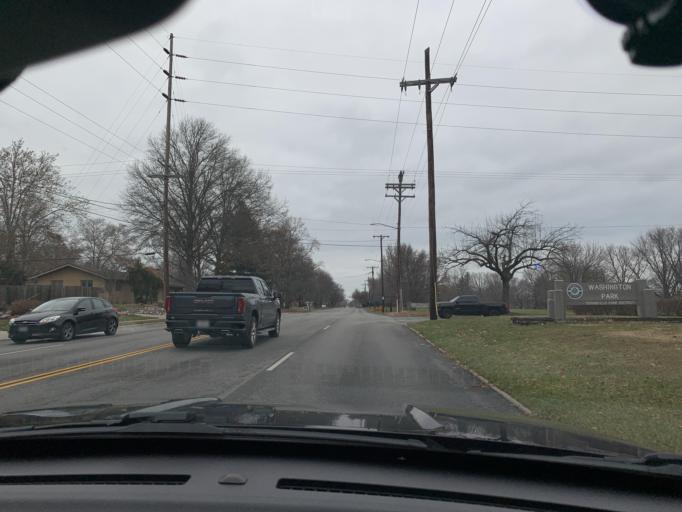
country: US
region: Illinois
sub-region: Sangamon County
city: Leland Grove
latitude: 39.7901
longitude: -89.6869
